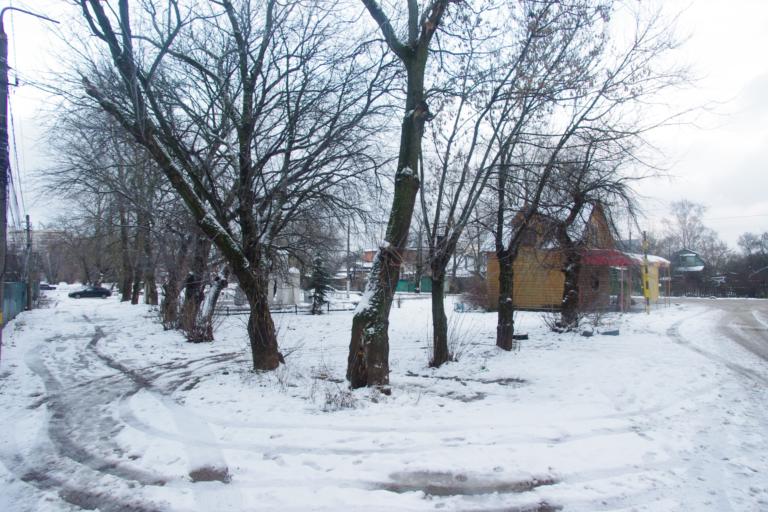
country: RU
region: Moskovskaya
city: Pavshino
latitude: 55.8107
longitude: 37.3538
